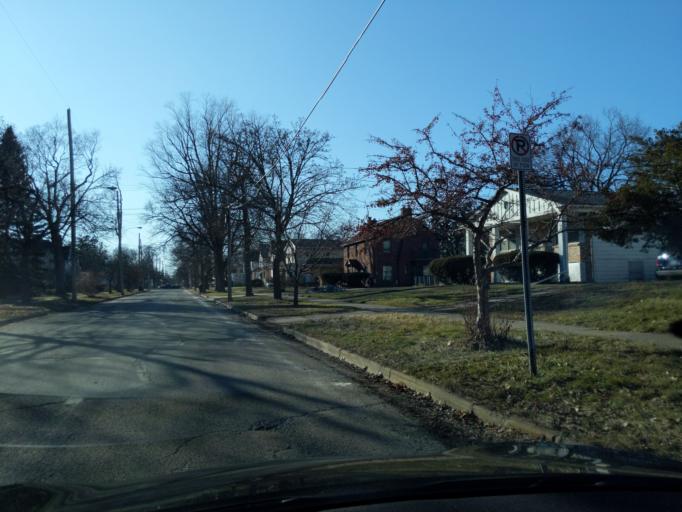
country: US
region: Michigan
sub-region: Ingham County
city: Lansing
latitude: 42.7360
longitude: -84.5648
